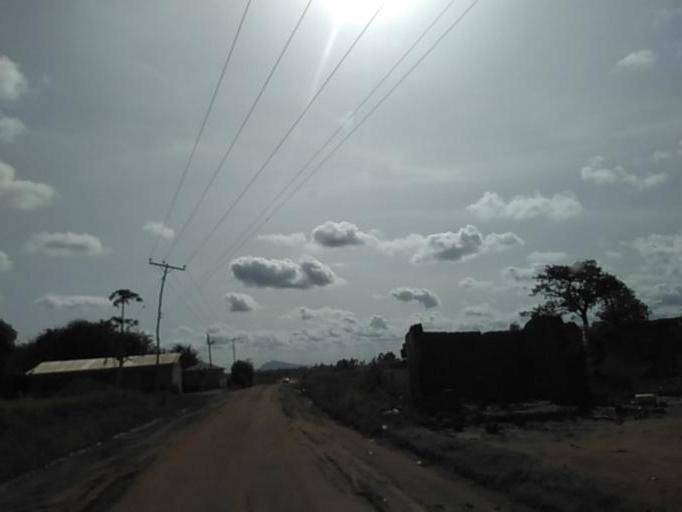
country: GH
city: Akropong
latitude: 6.0295
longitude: 0.3650
